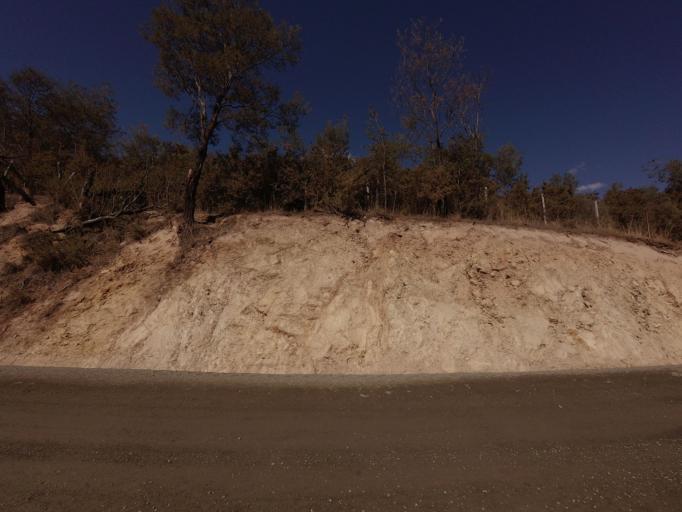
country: AU
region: Tasmania
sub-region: Break O'Day
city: St Helens
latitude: -41.6535
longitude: 147.9245
